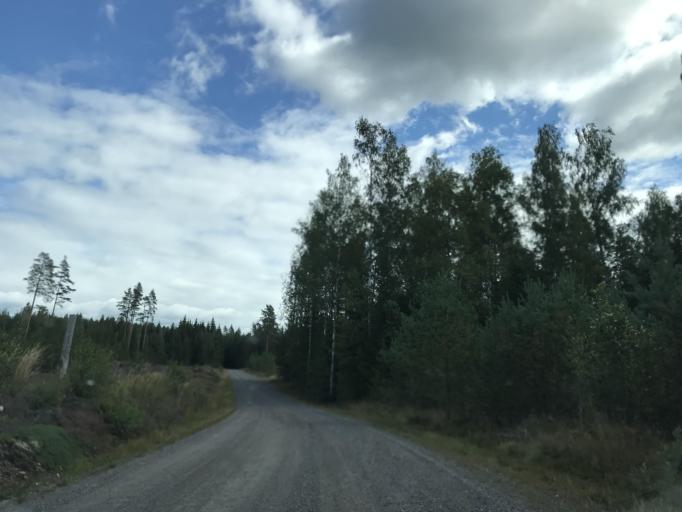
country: FI
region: Uusimaa
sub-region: Helsinki
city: Kaerkoelae
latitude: 60.6350
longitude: 23.7919
